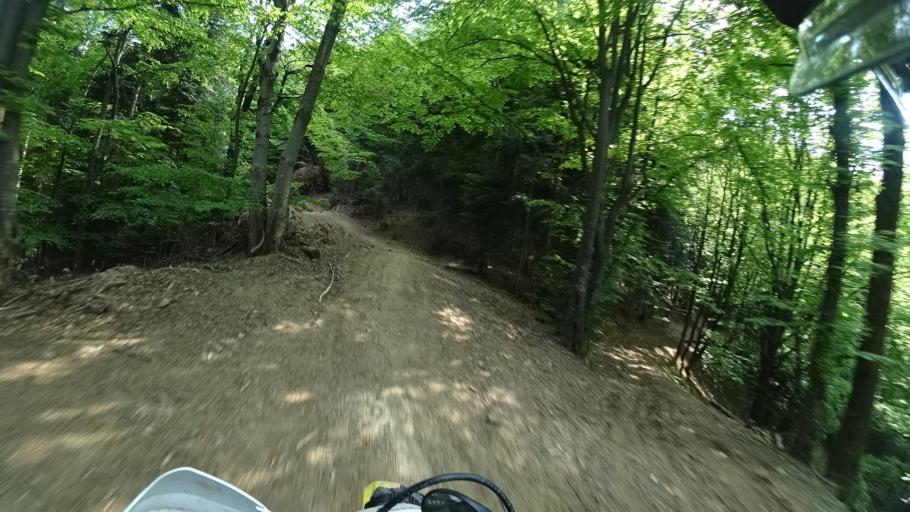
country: HR
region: Grad Zagreb
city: Kasina
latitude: 45.9255
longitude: 15.9505
